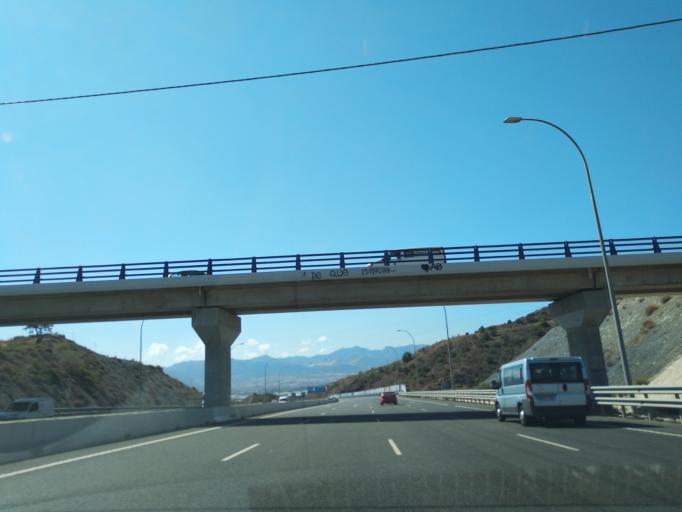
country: ES
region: Andalusia
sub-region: Provincia de Malaga
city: Malaga
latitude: 36.7381
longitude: -4.5046
